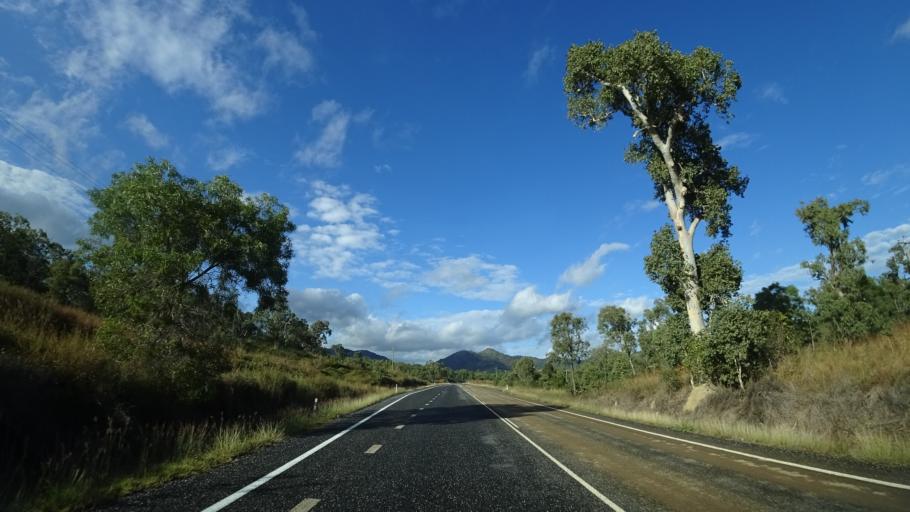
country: AU
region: Queensland
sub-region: Cook
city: Cooktown
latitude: -15.6122
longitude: 145.2213
